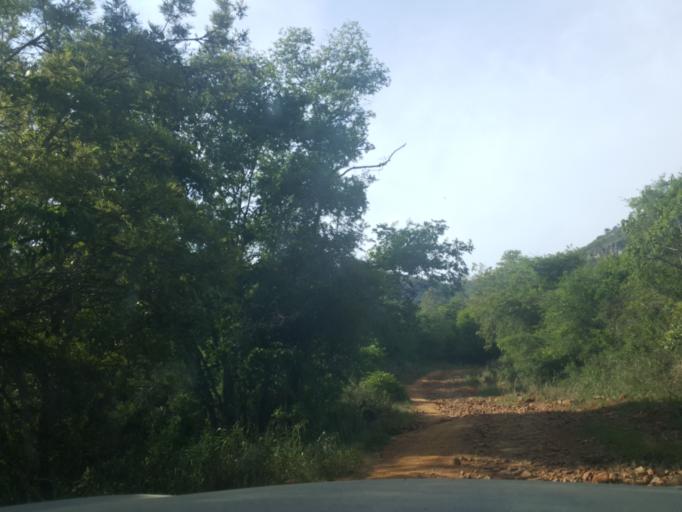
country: ZA
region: Limpopo
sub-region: Mopani District Municipality
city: Hoedspruit
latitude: -24.5916
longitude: 30.8288
